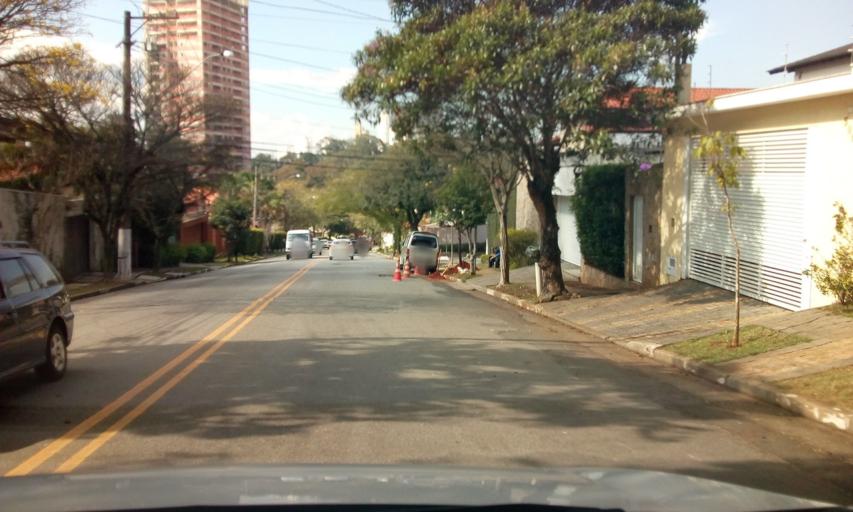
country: BR
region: Sao Paulo
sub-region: Osasco
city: Osasco
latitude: -23.5598
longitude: -46.7697
